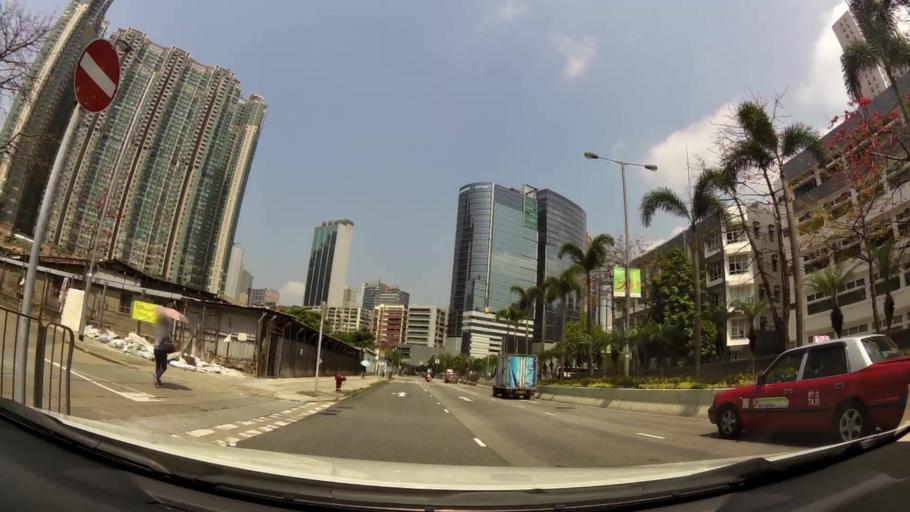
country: HK
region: Sham Shui Po
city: Sham Shui Po
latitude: 22.3348
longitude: 114.1523
